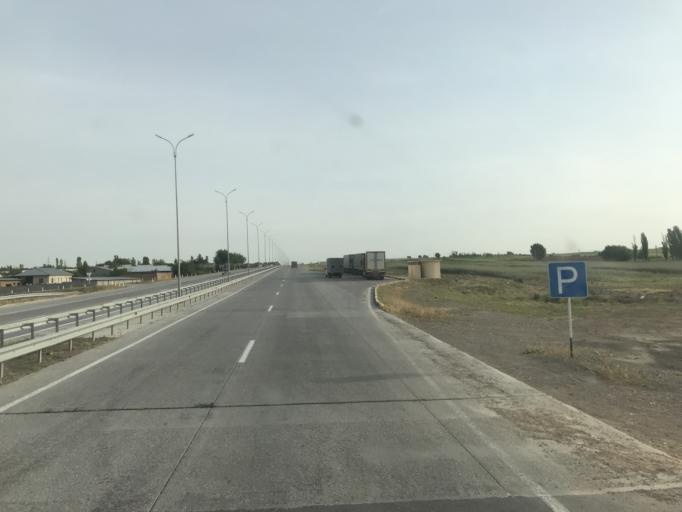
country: UZ
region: Toshkent
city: Qibray
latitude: 41.5550
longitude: 69.4077
